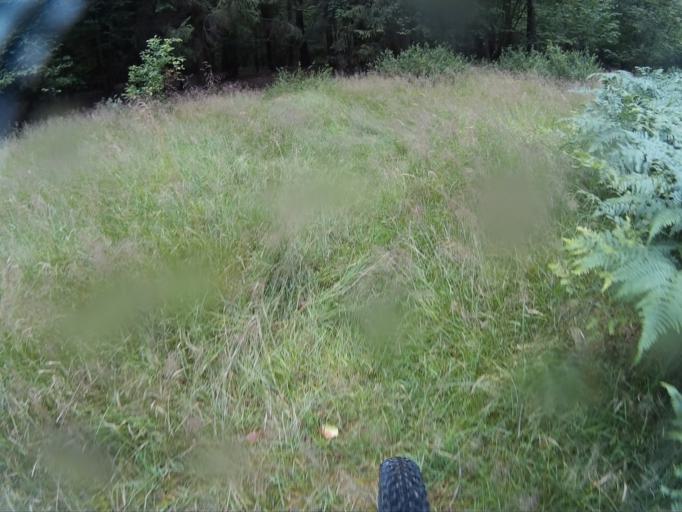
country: PL
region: Kujawsko-Pomorskie
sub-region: Powiat tucholski
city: Tuchola
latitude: 53.5820
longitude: 17.9071
